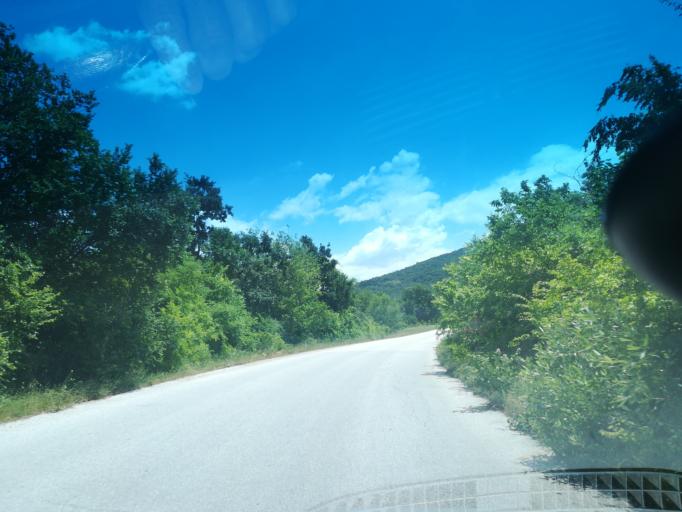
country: BG
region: Khaskovo
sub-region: Obshtina Mineralni Bani
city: Mineralni Bani
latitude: 41.9809
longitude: 25.2469
